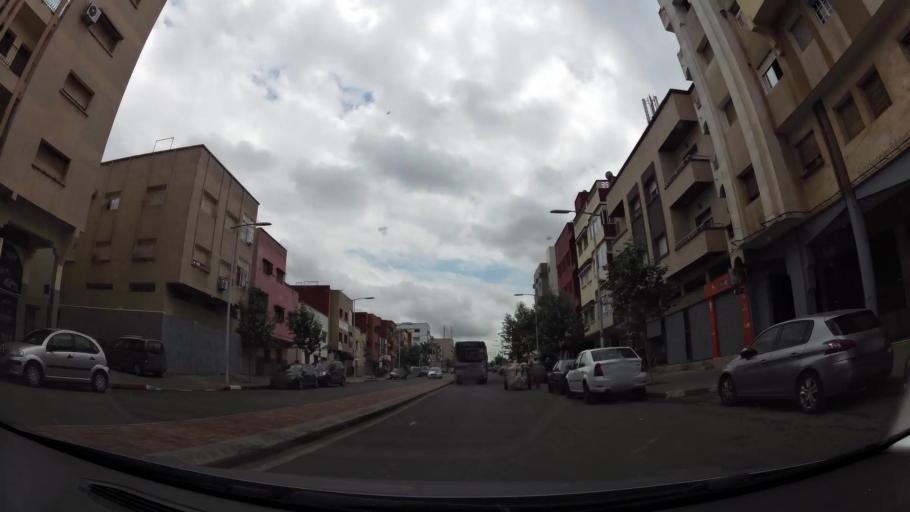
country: MA
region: Rabat-Sale-Zemmour-Zaer
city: Sale
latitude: 34.0384
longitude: -6.8084
